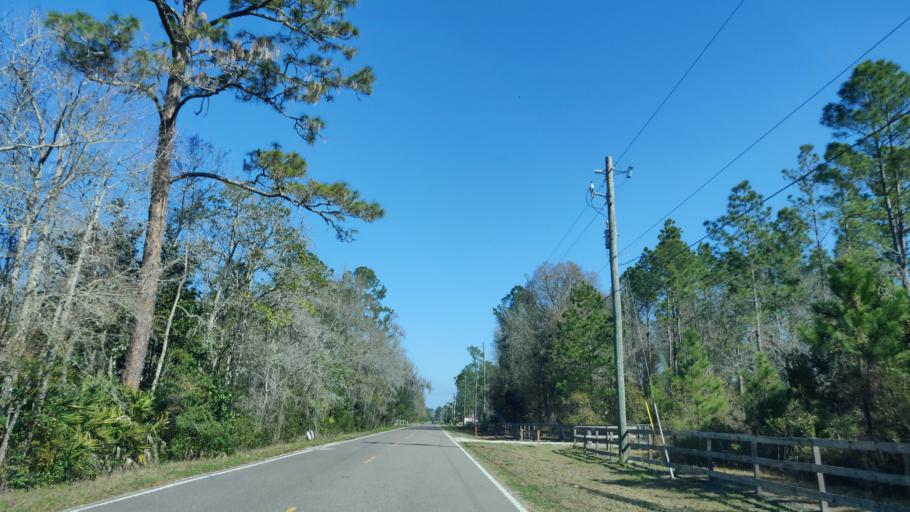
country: US
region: Florida
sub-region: Duval County
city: Baldwin
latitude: 30.1962
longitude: -81.9660
